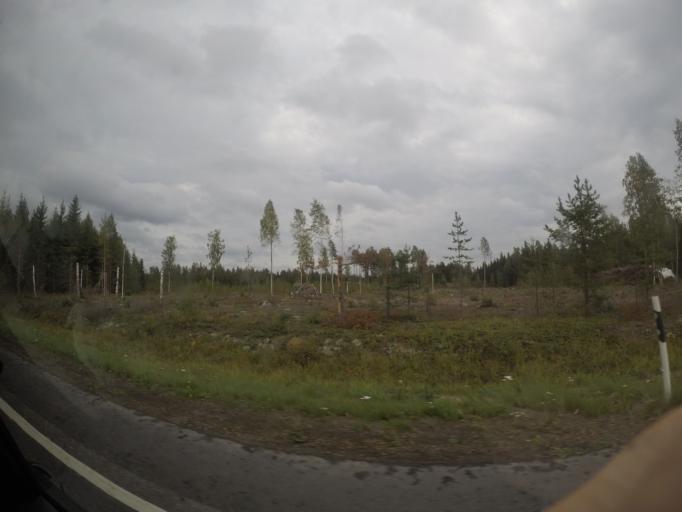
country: FI
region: Haeme
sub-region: Haemeenlinna
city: Parola
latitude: 61.1374
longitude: 24.4162
